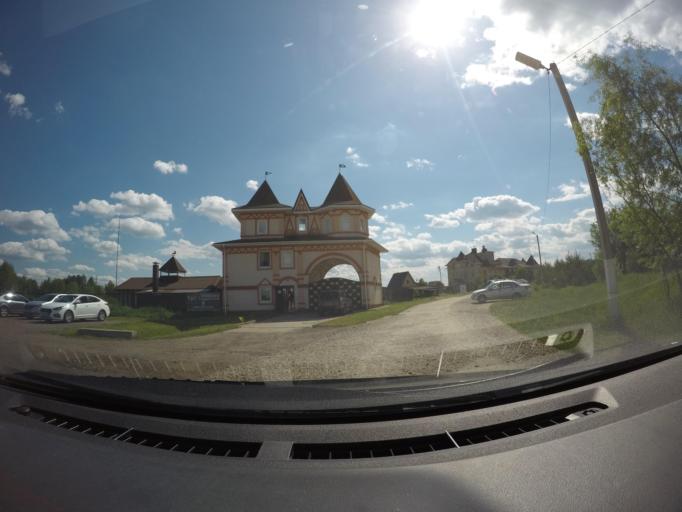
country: RU
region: Moskovskaya
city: Rechitsy
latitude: 55.5773
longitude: 38.5068
